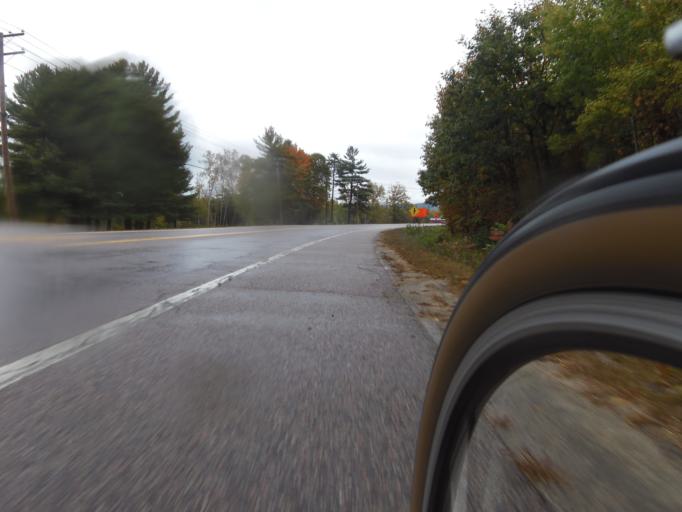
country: CA
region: Quebec
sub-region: Outaouais
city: Fort-Coulonge
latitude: 45.8558
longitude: -76.7391
